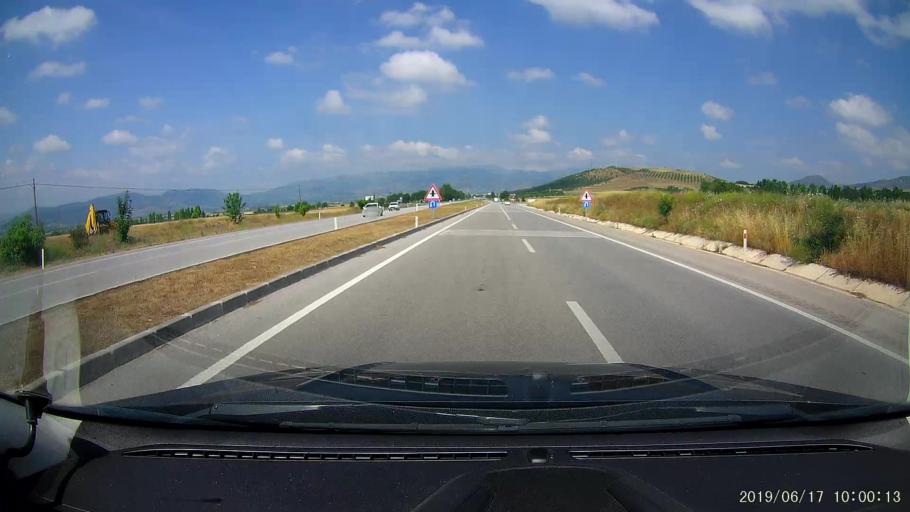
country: TR
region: Amasya
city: Alicik
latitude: 40.8664
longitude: 35.2934
